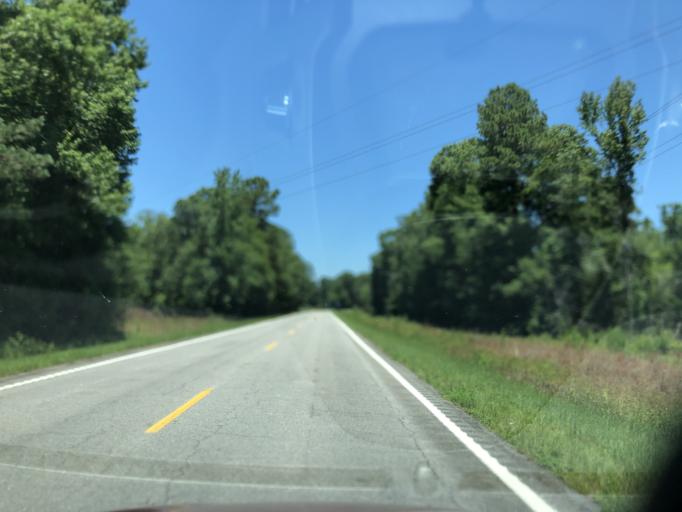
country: US
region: South Carolina
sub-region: Orangeburg County
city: Branchville
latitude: 33.2272
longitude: -80.8862
